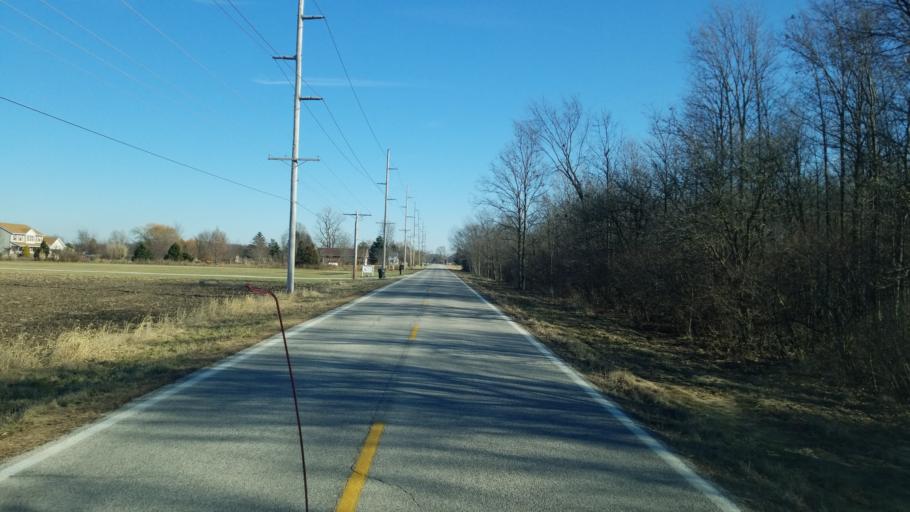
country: US
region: Ohio
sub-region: Sandusky County
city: Woodville
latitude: 41.4493
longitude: -83.4027
